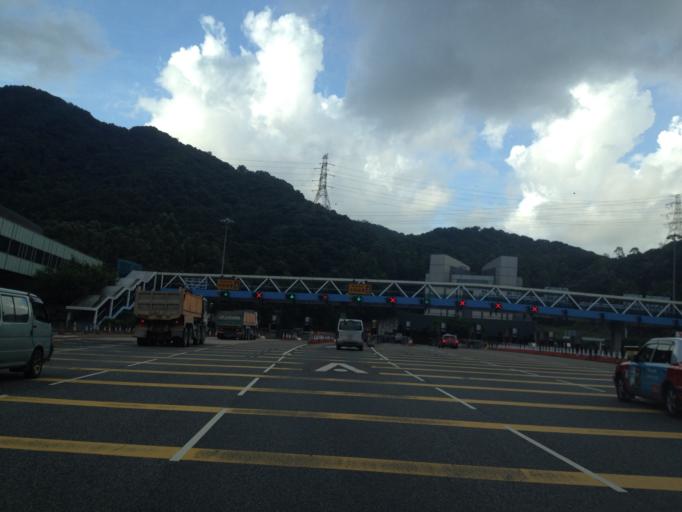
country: HK
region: Wong Tai Sin
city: Wong Tai Sin
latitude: 22.3604
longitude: 114.1636
